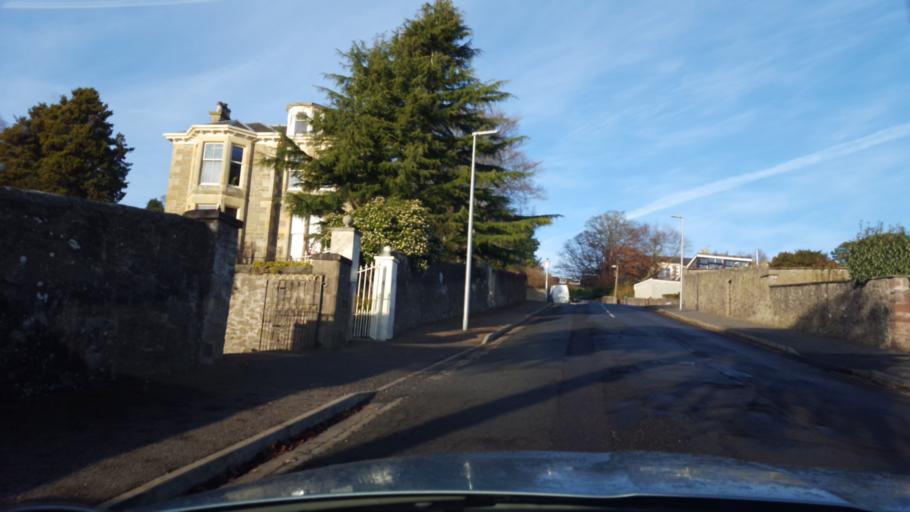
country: GB
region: Scotland
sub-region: Fife
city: Tayport
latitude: 56.4697
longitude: -2.8646
